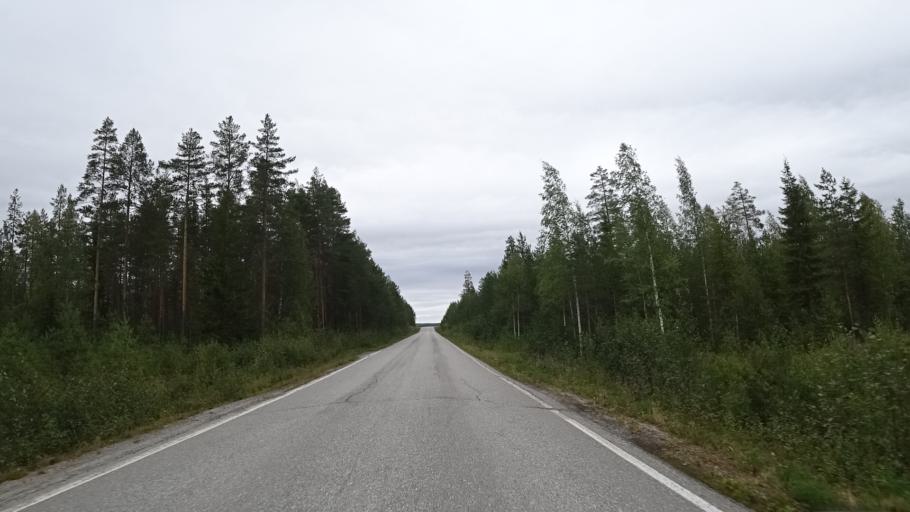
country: FI
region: North Karelia
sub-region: Pielisen Karjala
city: Lieksa
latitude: 63.3765
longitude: 30.3083
